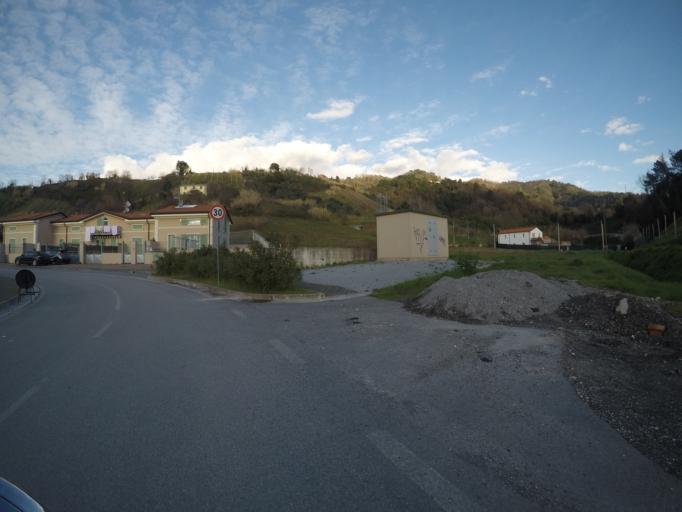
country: IT
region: Tuscany
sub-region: Provincia di Massa-Carrara
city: Carrara
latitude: 44.0609
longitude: 10.0876
